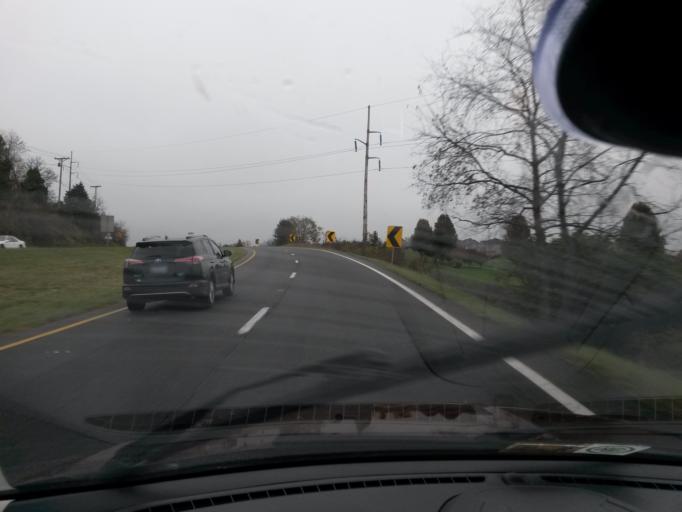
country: US
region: Virginia
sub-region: Botetourt County
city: Daleville
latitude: 37.4289
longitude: -79.9042
